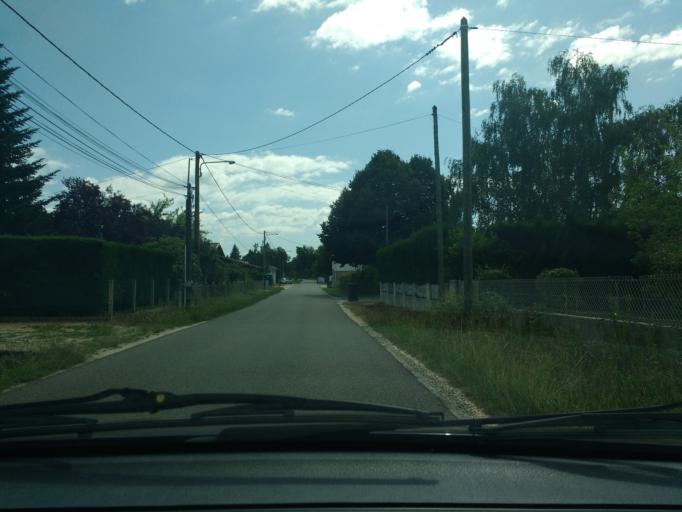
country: FR
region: Aquitaine
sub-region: Departement de la Gironde
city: Salles
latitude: 44.5597
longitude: -0.8551
